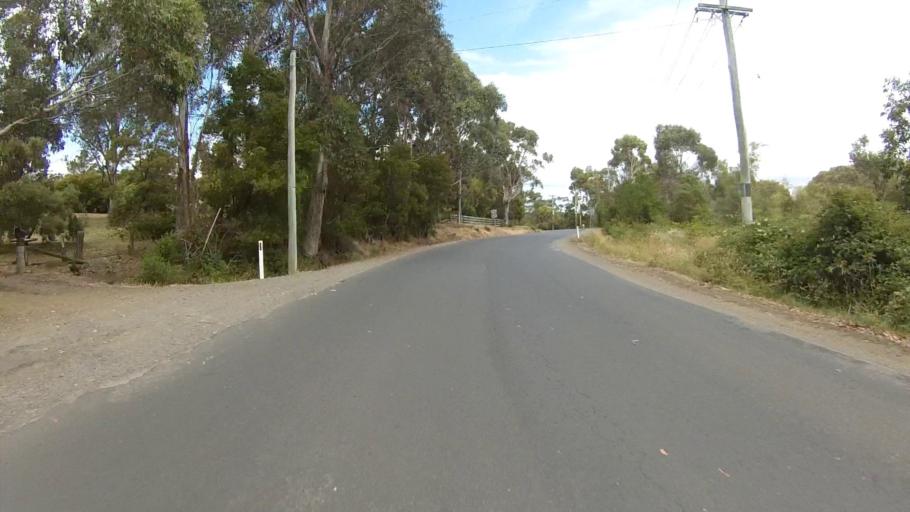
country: AU
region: Tasmania
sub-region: Kingborough
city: Blackmans Bay
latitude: -43.0153
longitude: 147.2915
